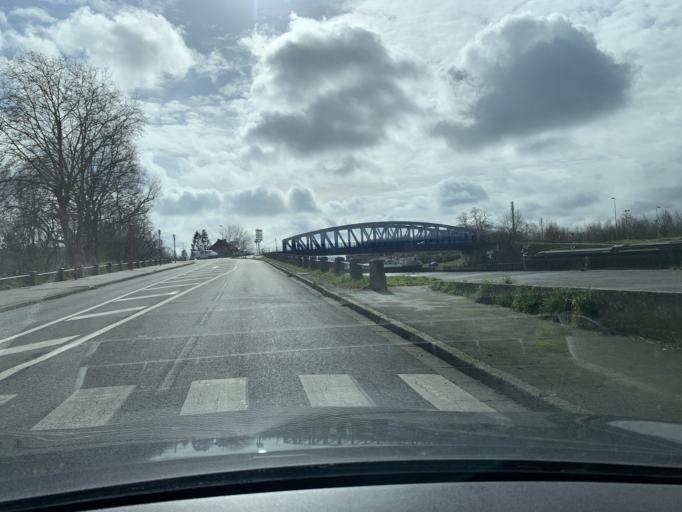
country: FR
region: Nord-Pas-de-Calais
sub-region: Departement du Nord
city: Flers-en-Escrebieux
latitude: 50.3918
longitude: 3.0807
